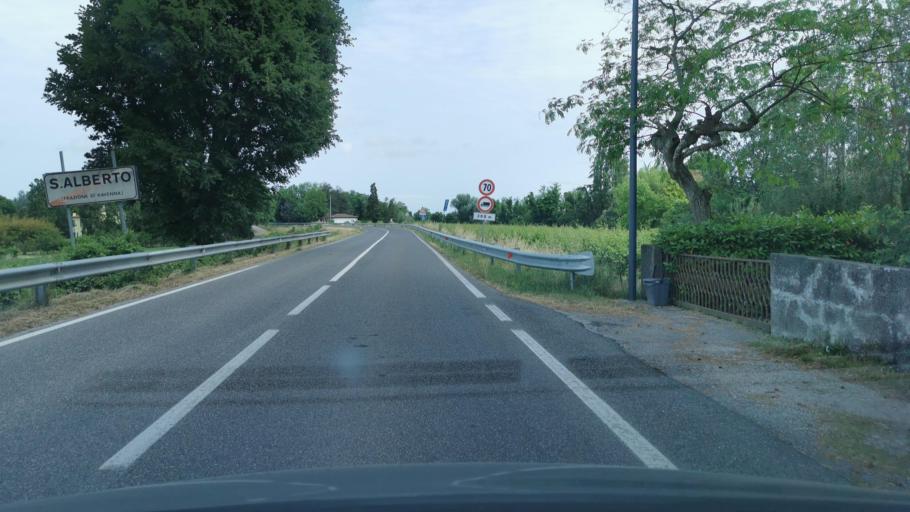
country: IT
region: Emilia-Romagna
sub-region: Provincia di Ravenna
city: Sant'Alberto
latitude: 44.5357
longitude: 12.1721
